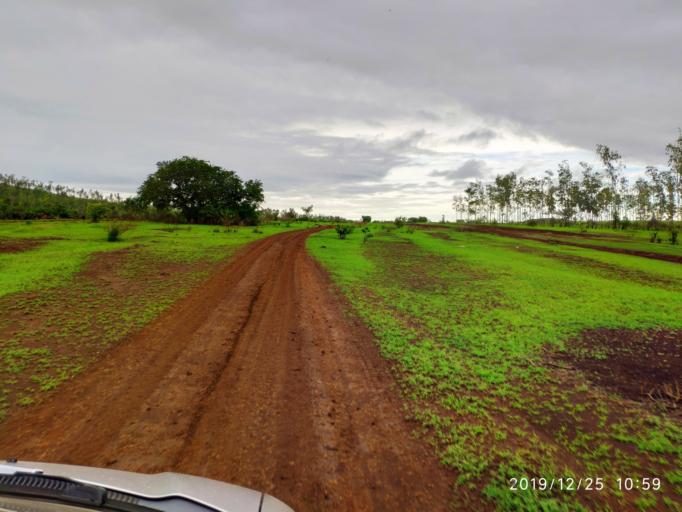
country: MG
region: Diana
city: Sadjoavato
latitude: -12.8057
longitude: 49.2405
